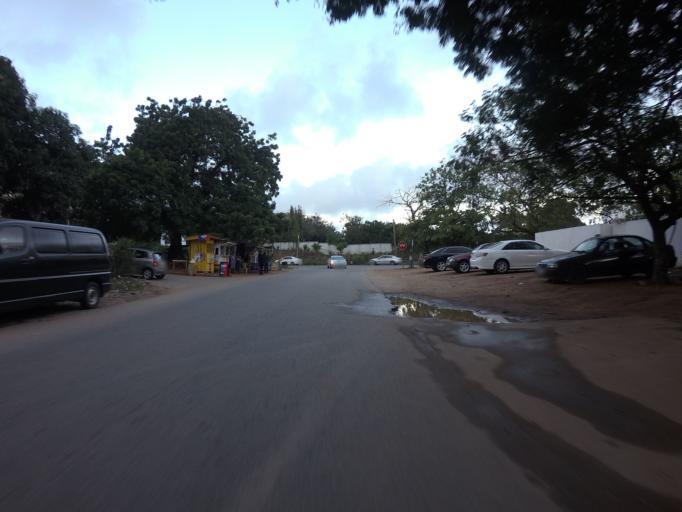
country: GH
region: Greater Accra
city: Accra
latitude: 5.5722
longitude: -0.1846
